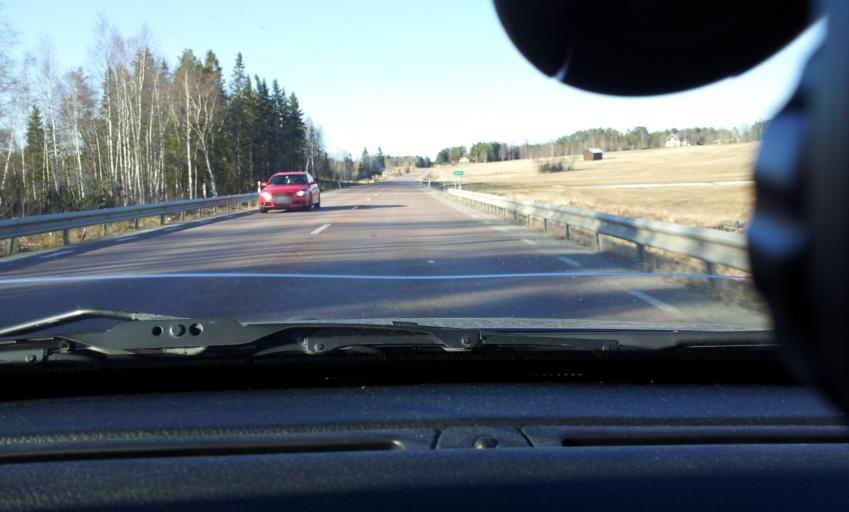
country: SE
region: Jaemtland
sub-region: Bergs Kommun
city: Hoverberg
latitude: 62.9703
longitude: 14.5597
